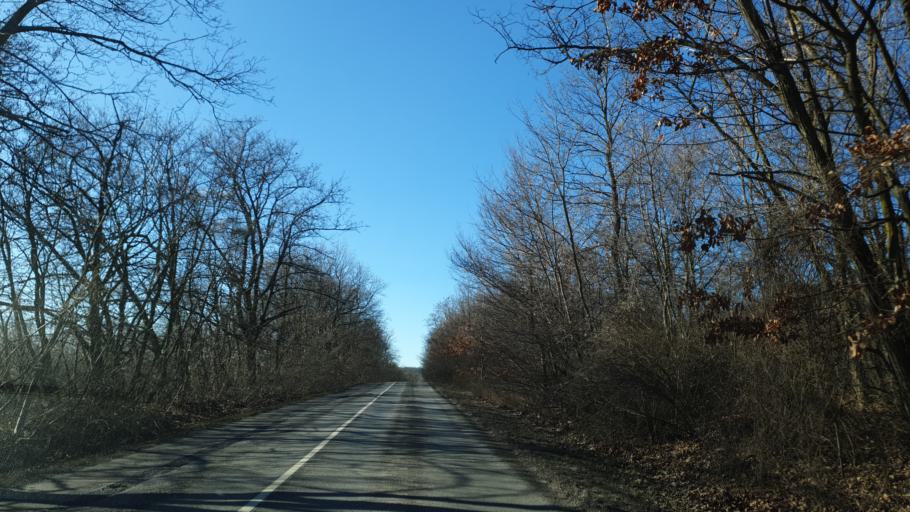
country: HU
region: Pest
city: Budakeszi
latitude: 47.5039
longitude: 18.9009
